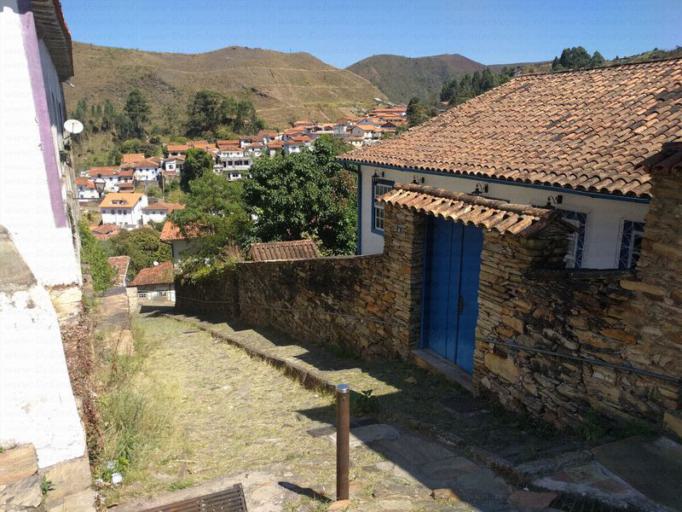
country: BR
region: Minas Gerais
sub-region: Ouro Preto
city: Ouro Preto
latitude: -20.3849
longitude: -43.5087
